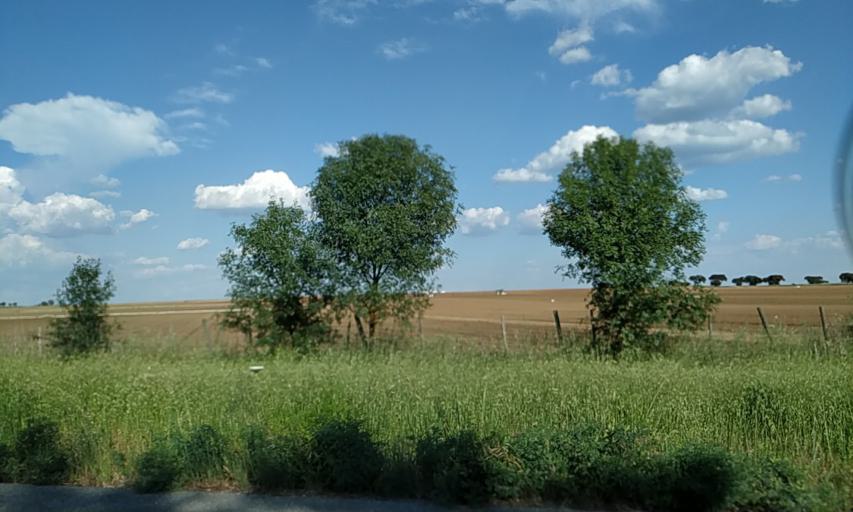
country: PT
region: Evora
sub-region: Estremoz
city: Estremoz
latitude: 38.9809
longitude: -7.4838
